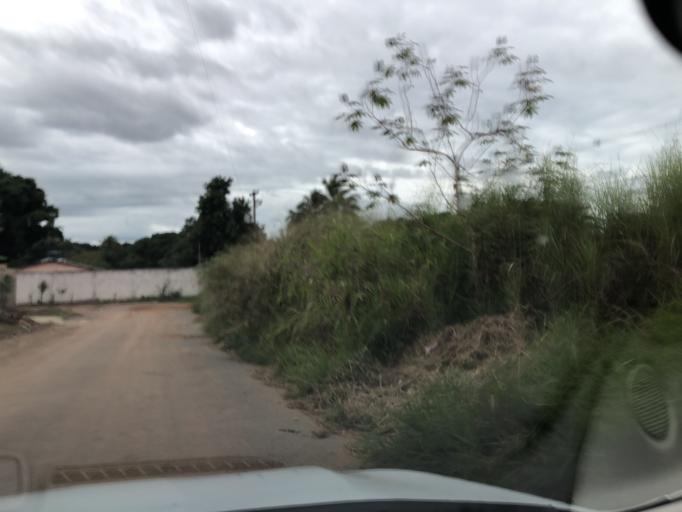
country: BR
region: Goias
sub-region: Luziania
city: Luziania
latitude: -16.1601
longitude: -47.9498
